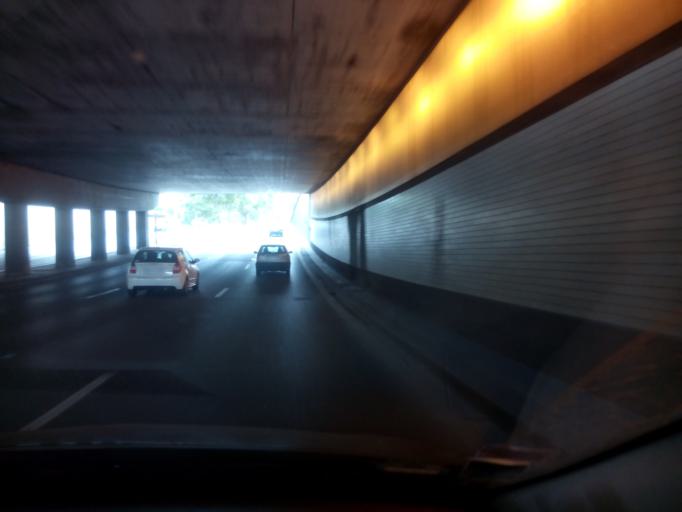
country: FR
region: Ile-de-France
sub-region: Departement du Val-de-Marne
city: Ivry-sur-Seine
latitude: 48.8339
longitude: 2.3818
